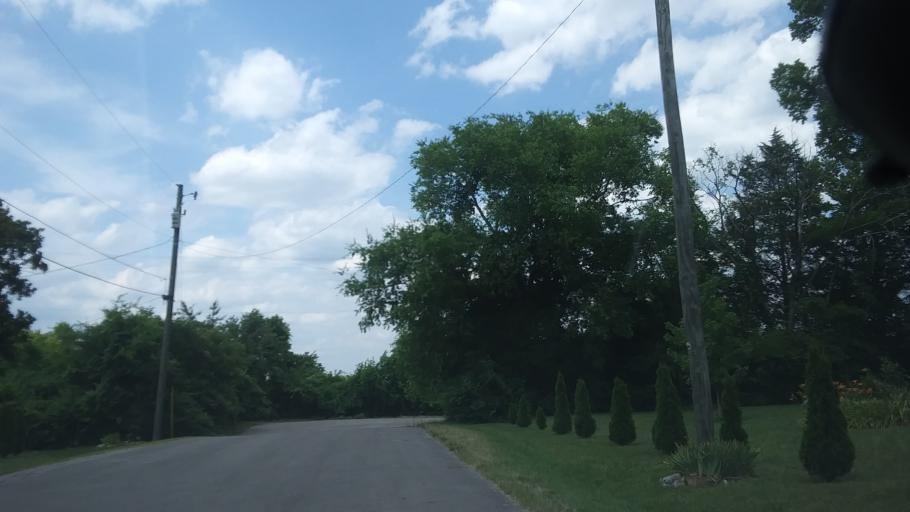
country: US
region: Tennessee
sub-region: Davidson County
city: Oak Hill
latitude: 36.0832
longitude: -86.6928
